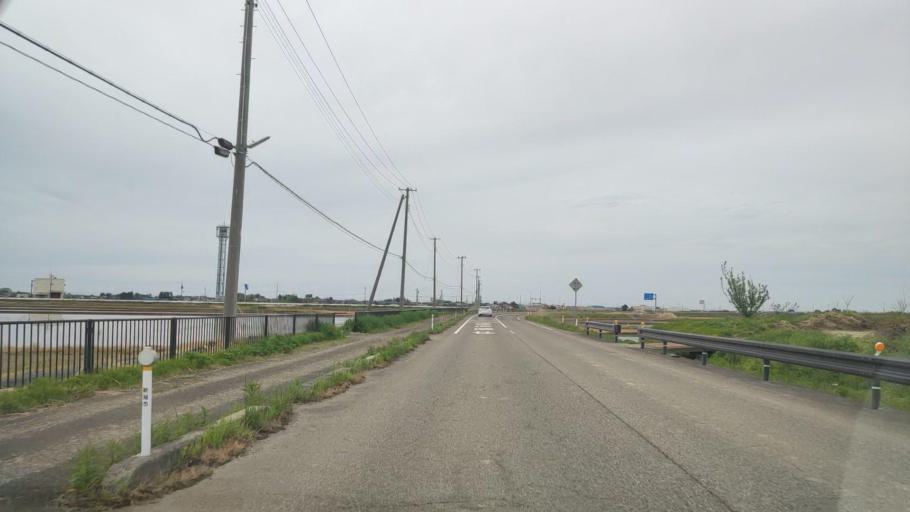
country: JP
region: Niigata
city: Shirone
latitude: 37.7358
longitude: 139.0805
